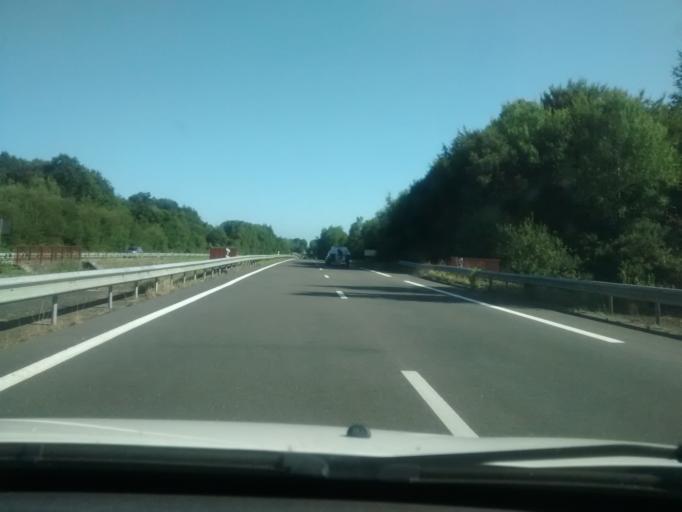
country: FR
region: Brittany
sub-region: Departement d'Ille-et-Vilaine
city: Miniac-Morvan
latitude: 48.4847
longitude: -1.9080
